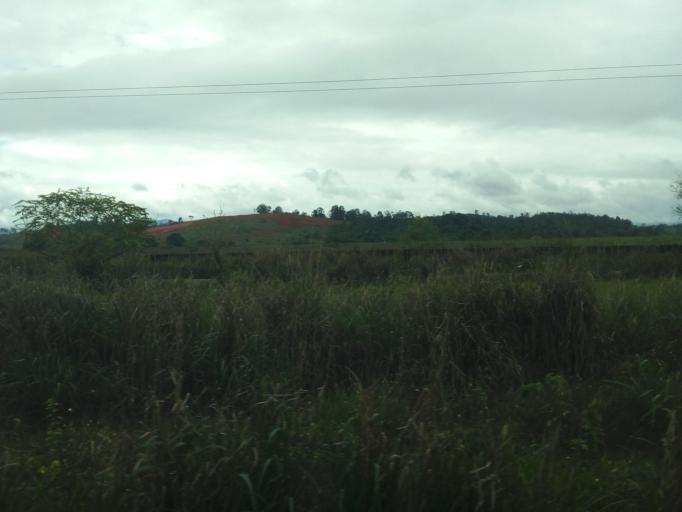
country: BR
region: Minas Gerais
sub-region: Ipatinga
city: Ipatinga
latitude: -19.4690
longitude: -42.4800
